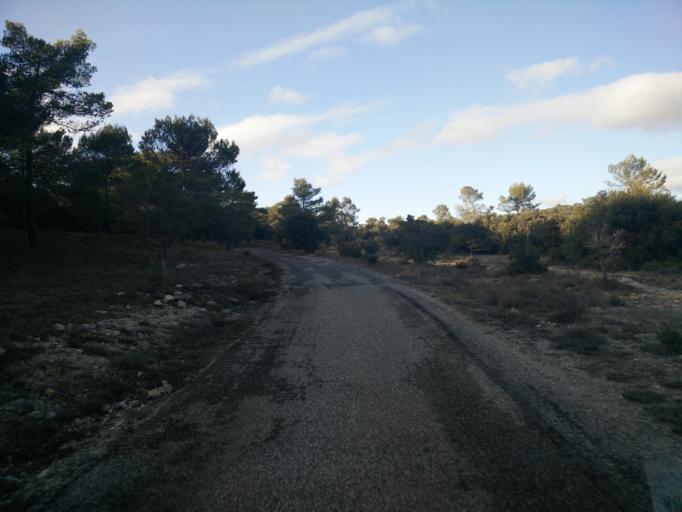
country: FR
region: Provence-Alpes-Cote d'Azur
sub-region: Departement du Var
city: Le Revest-les-Eaux
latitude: 43.2296
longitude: 5.9129
